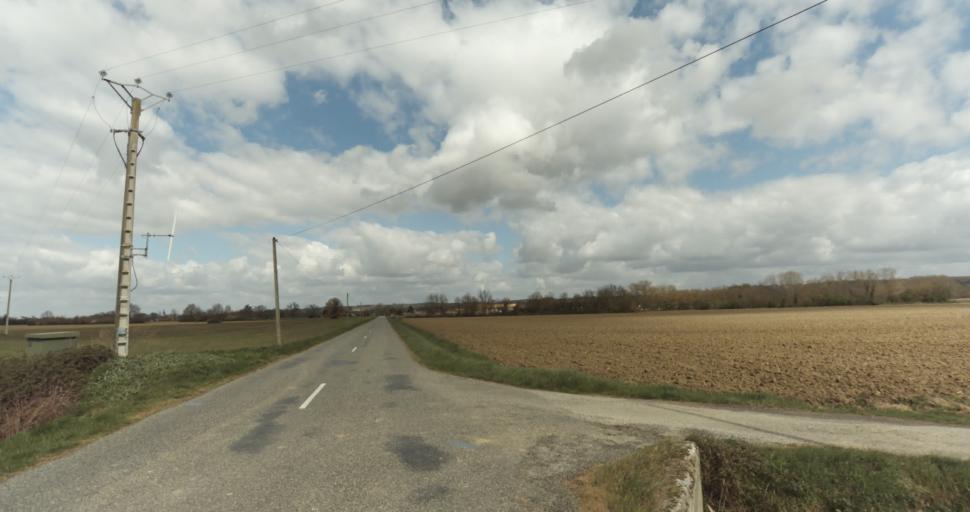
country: FR
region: Midi-Pyrenees
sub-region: Departement de la Haute-Garonne
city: Auterive
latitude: 43.3287
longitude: 1.4776
